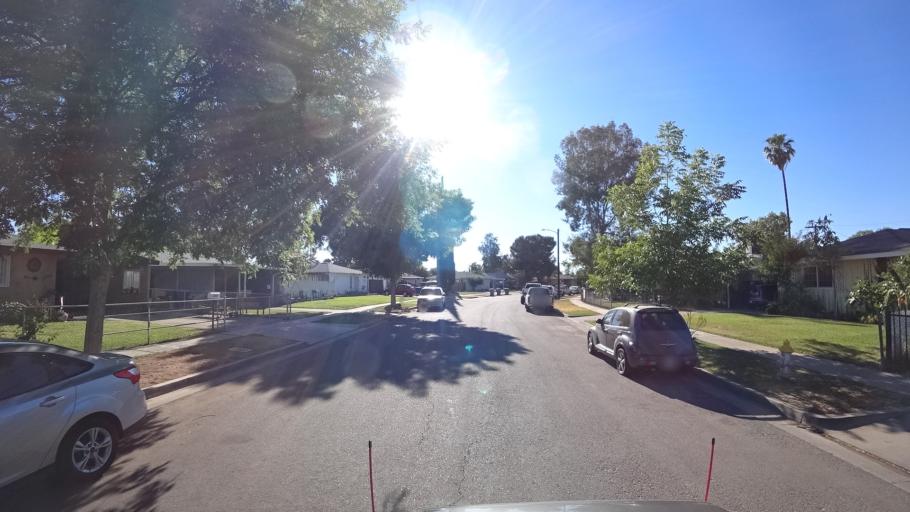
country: US
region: California
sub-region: Fresno County
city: Fresno
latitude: 36.7950
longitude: -119.8245
